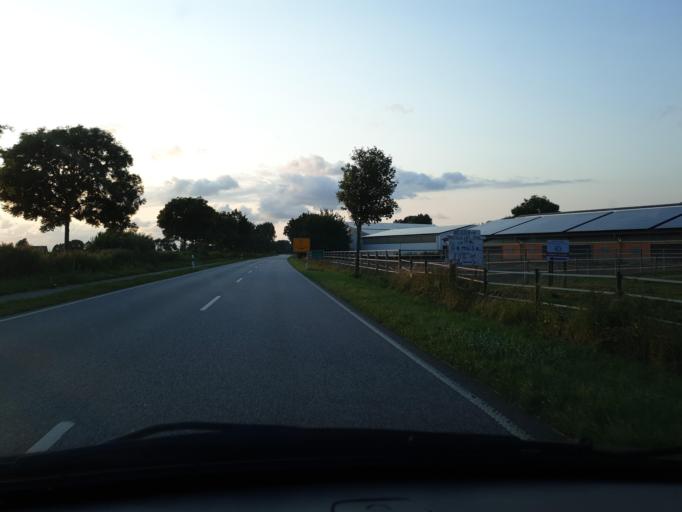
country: DE
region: Schleswig-Holstein
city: Schmedeswurth
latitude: 53.9148
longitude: 9.0510
